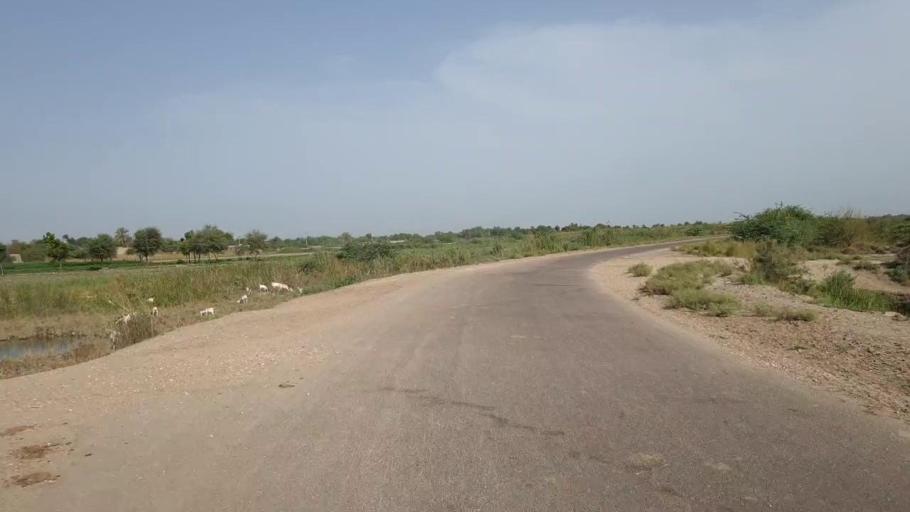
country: PK
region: Sindh
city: Sakrand
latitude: 26.2722
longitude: 68.2740
